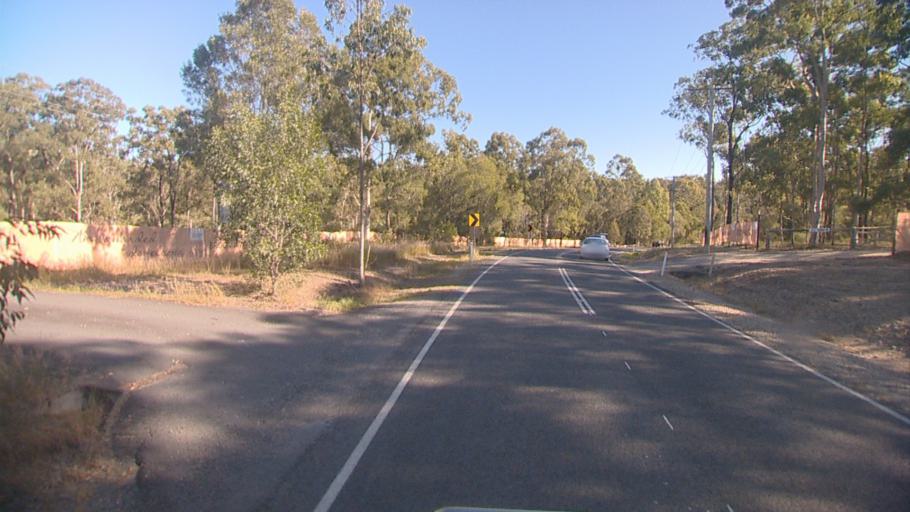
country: AU
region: Queensland
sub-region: Logan
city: Windaroo
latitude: -27.7345
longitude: 153.1617
